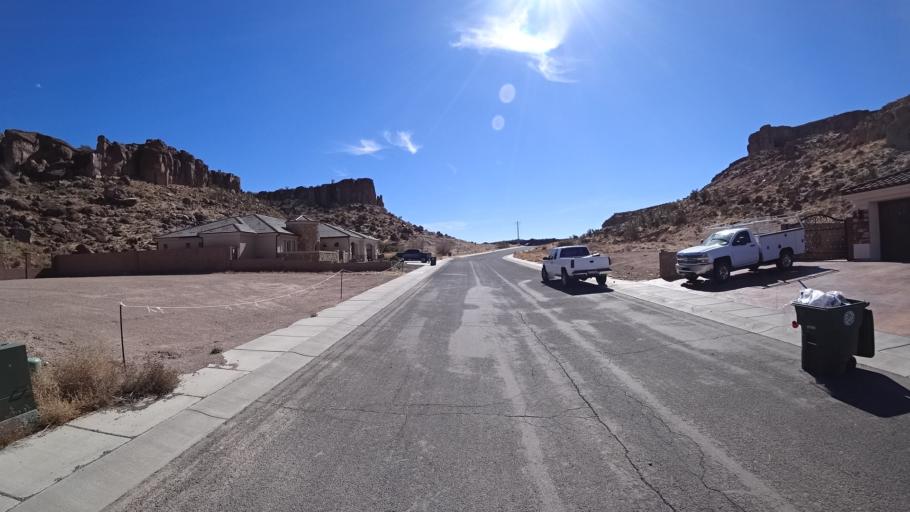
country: US
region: Arizona
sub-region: Mohave County
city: Kingman
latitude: 35.2080
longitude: -114.0552
